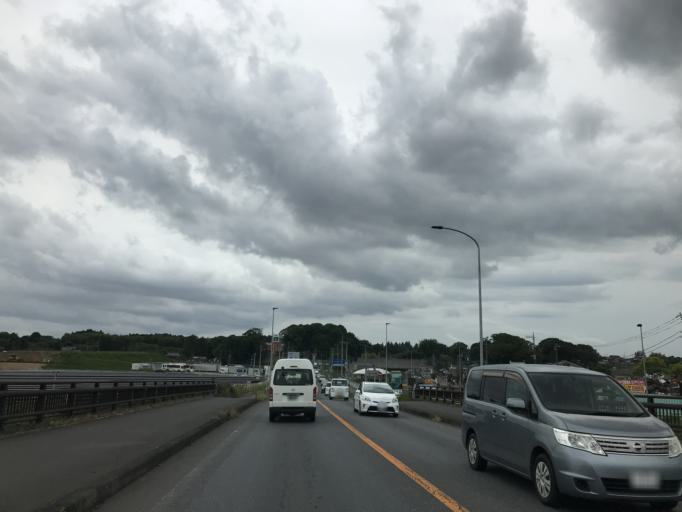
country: JP
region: Ibaraki
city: Ishioka
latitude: 36.1791
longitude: 140.2680
